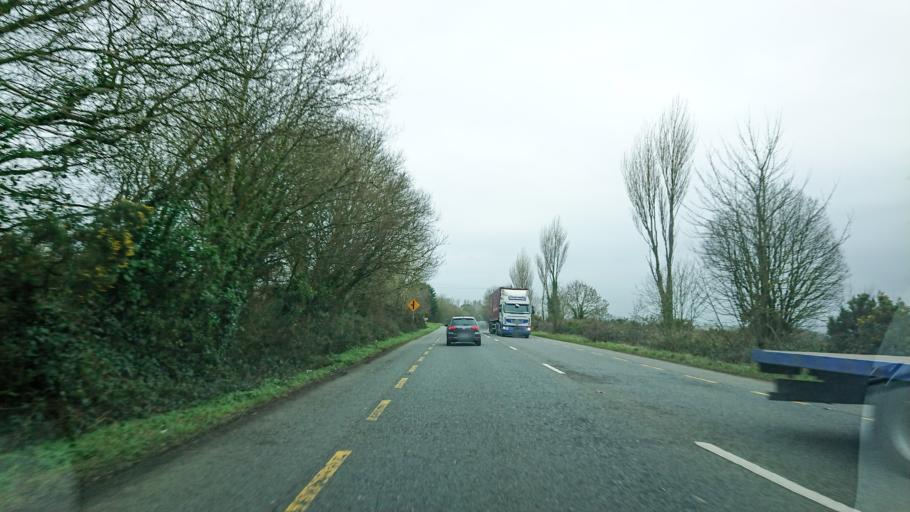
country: IE
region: Munster
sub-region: County Cork
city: Killumney
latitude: 51.7982
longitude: -8.5849
